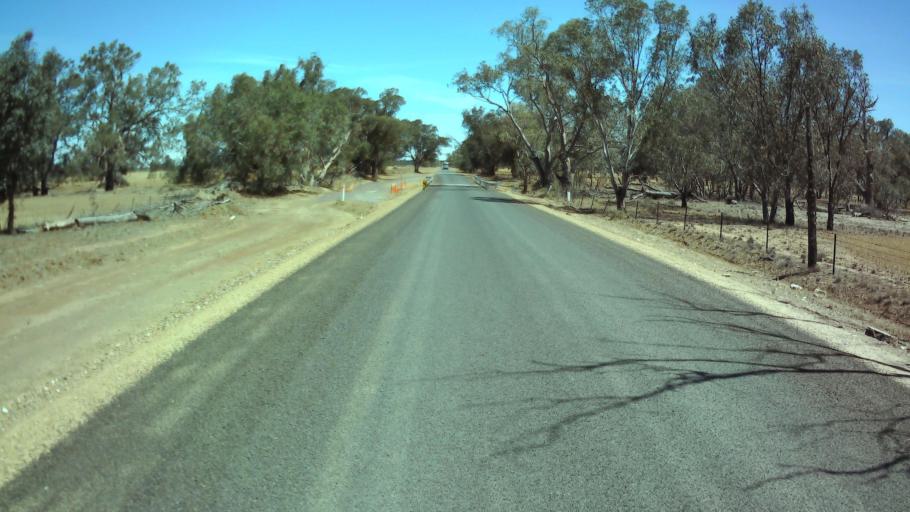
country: AU
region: New South Wales
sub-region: Weddin
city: Grenfell
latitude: -33.8424
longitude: 147.6971
